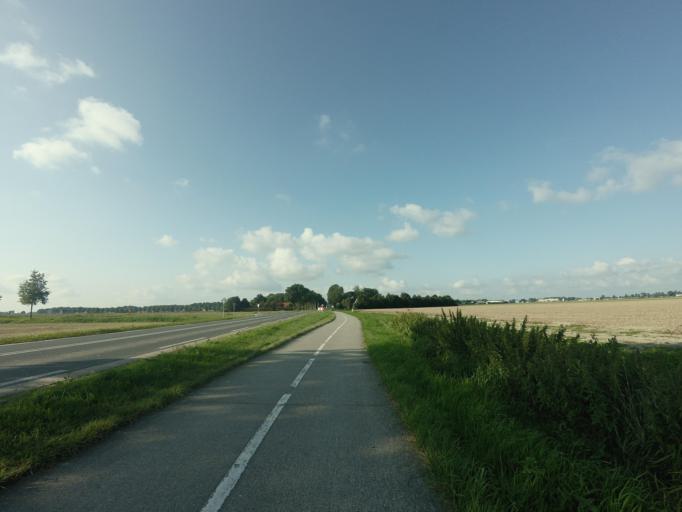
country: NL
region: Flevoland
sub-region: Gemeente Noordoostpolder
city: Ens
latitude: 52.6988
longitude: 5.8617
